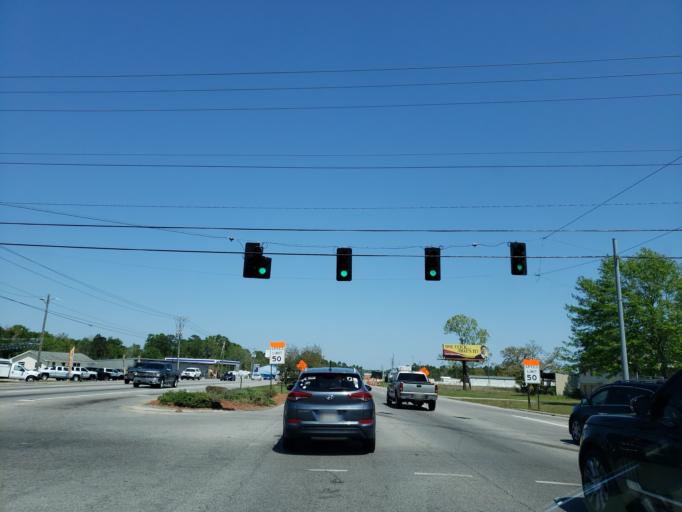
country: US
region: Mississippi
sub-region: Harrison County
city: Lyman
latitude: 30.4704
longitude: -89.1026
